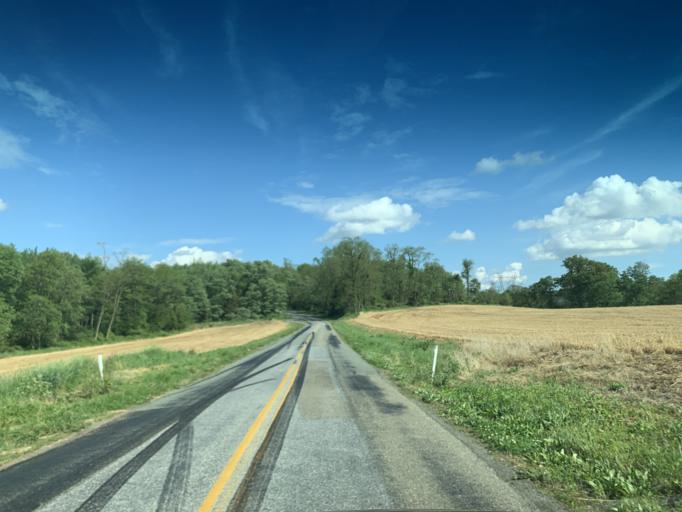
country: US
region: Maryland
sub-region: Cecil County
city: Rising Sun
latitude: 39.7224
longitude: -76.1790
